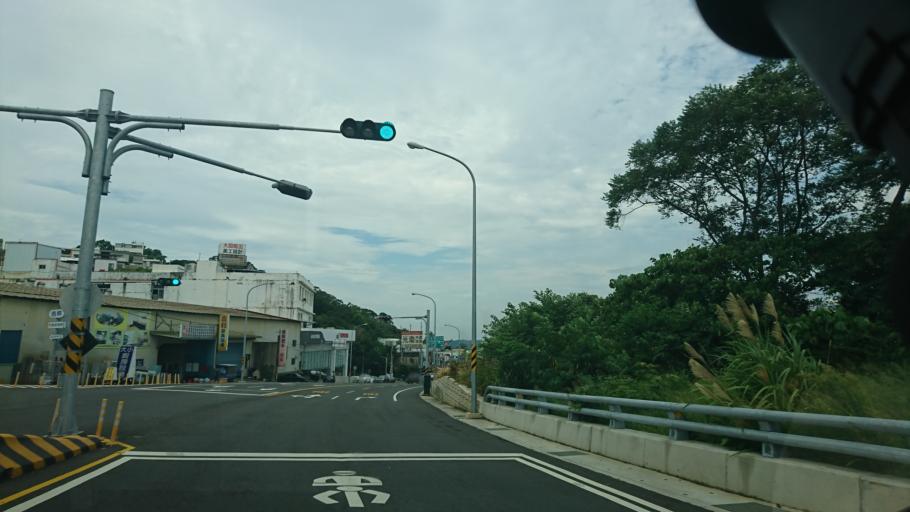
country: TW
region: Taiwan
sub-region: Miaoli
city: Miaoli
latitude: 24.5426
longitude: 120.8092
